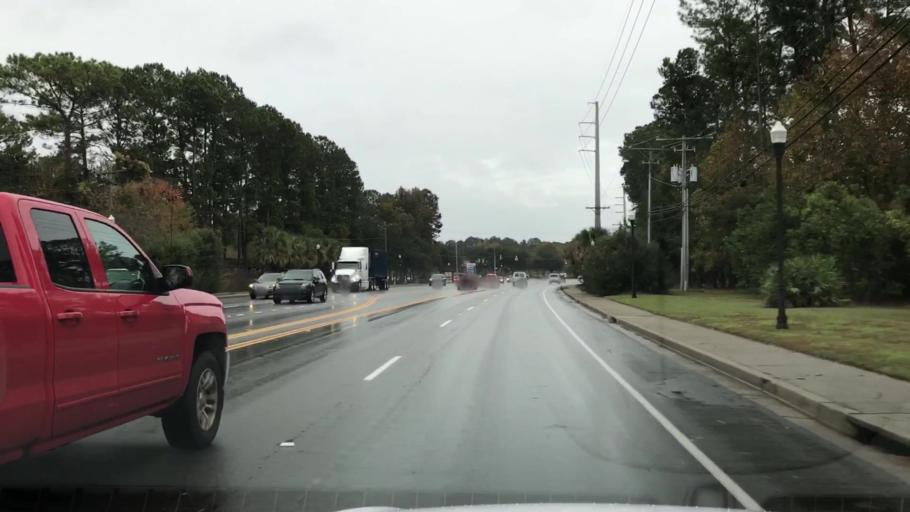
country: US
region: South Carolina
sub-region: Charleston County
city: Mount Pleasant
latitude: 32.8416
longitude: -79.8557
